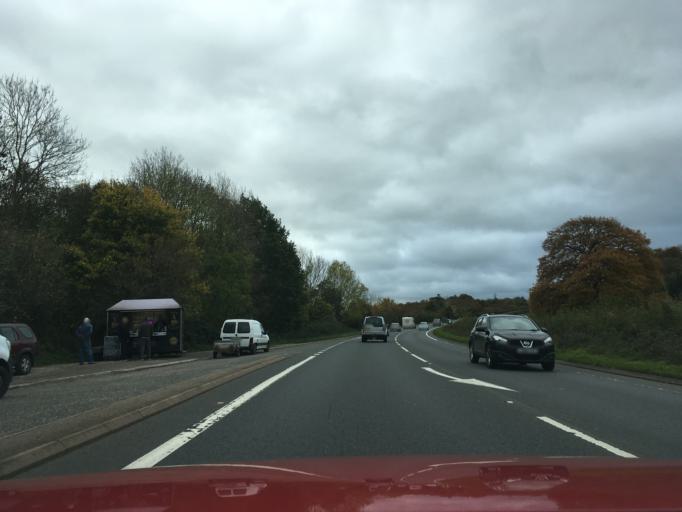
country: GB
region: England
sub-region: Somerset
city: Creech Saint Michael
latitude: 50.9886
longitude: -3.0085
